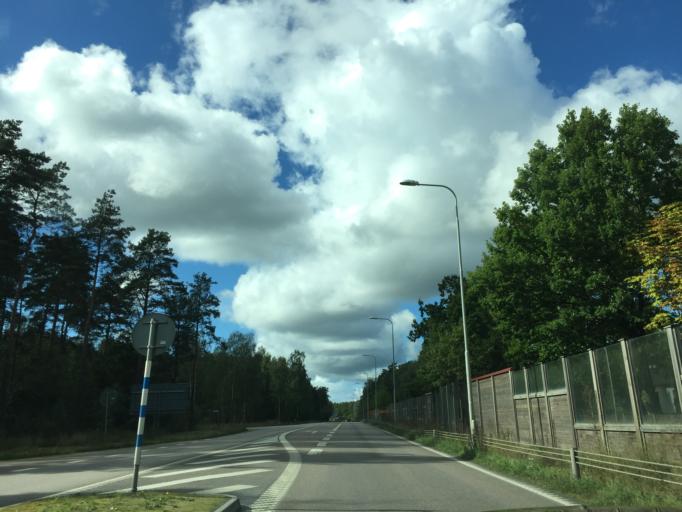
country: SE
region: Skane
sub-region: Sjobo Kommun
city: Sjoebo
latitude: 55.6346
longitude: 13.6767
